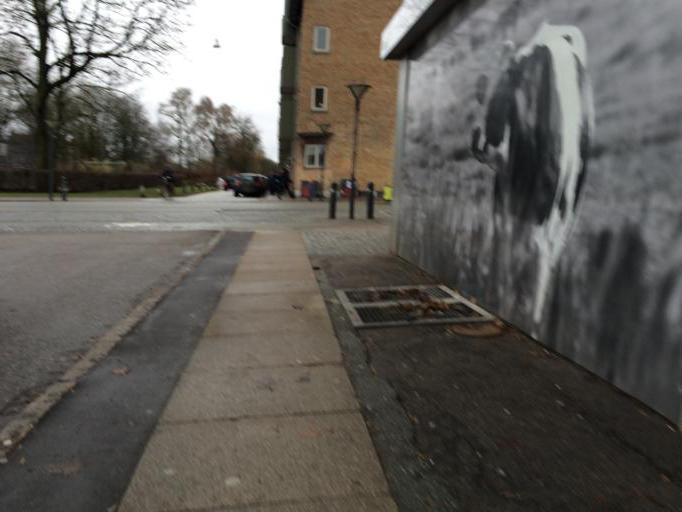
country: DK
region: Capital Region
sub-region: Frederiksberg Kommune
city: Frederiksberg
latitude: 55.6484
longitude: 12.5282
